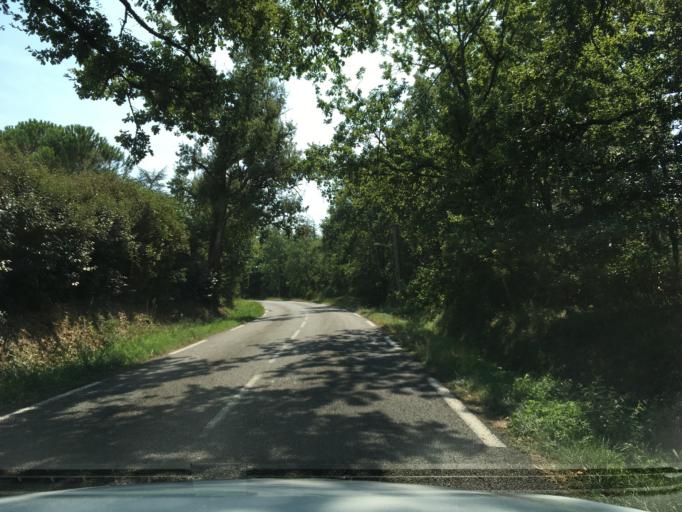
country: FR
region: Midi-Pyrenees
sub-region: Departement du Tarn-et-Garonne
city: Corbarieu
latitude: 43.9740
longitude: 1.3694
